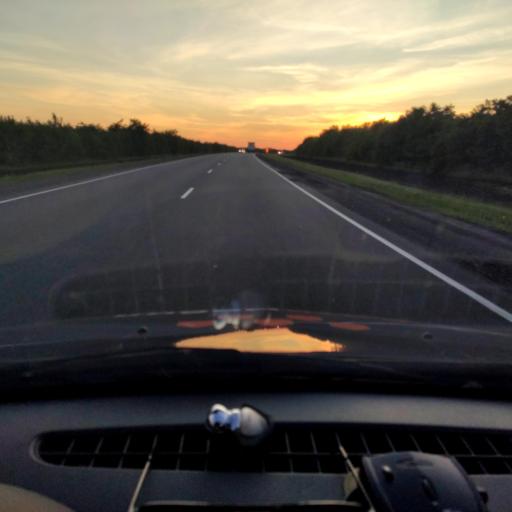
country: RU
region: Voronezj
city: Nizhnedevitsk
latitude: 51.5664
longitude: 38.3450
